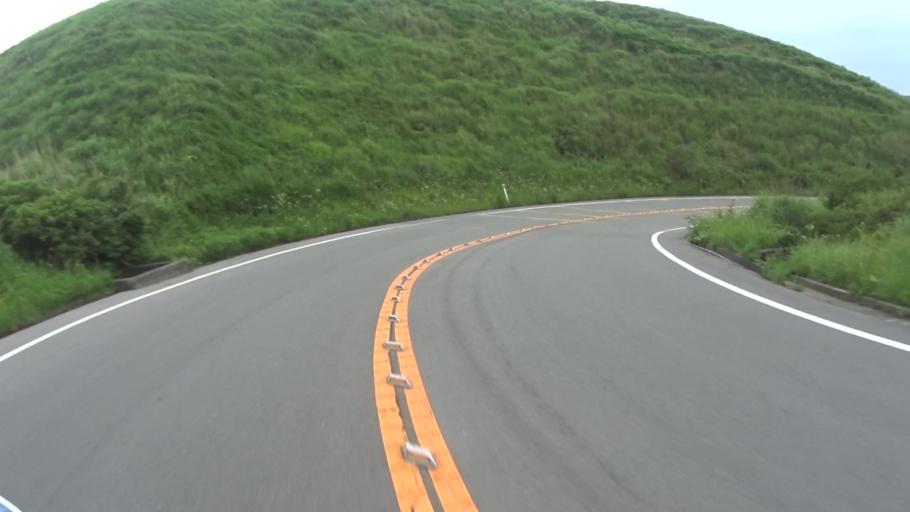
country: JP
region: Kumamoto
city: Ozu
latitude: 32.9152
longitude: 130.9648
